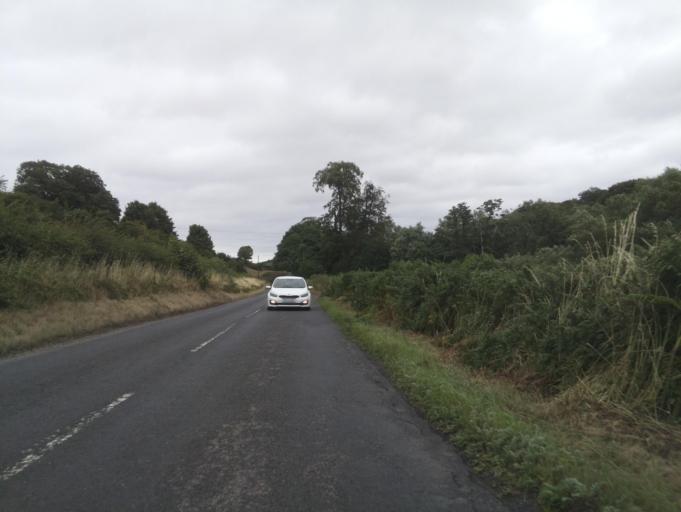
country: GB
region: England
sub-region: Derbyshire
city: Repton
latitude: 52.8186
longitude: -1.5401
